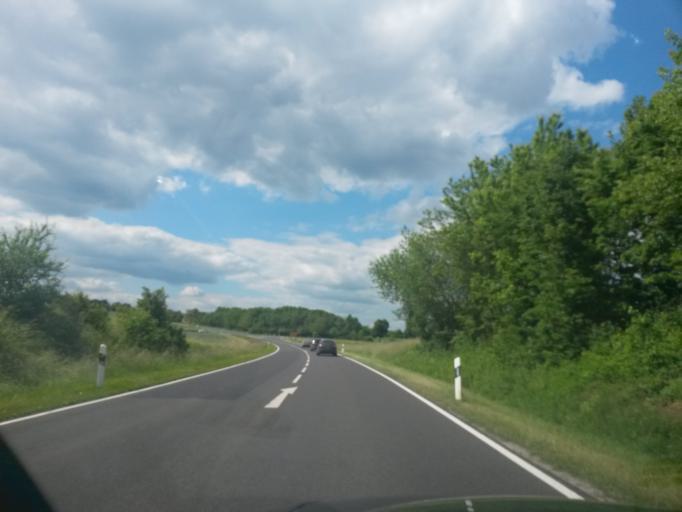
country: DE
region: Bavaria
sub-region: Regierungsbezirk Unterfranken
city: Estenfeld
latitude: 49.8362
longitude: 9.9886
